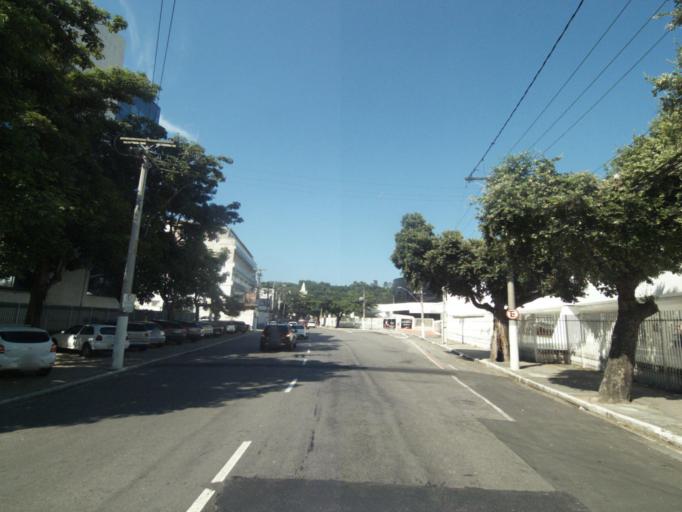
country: BR
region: Rio de Janeiro
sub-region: Niteroi
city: Niteroi
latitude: -22.8978
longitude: -43.1302
